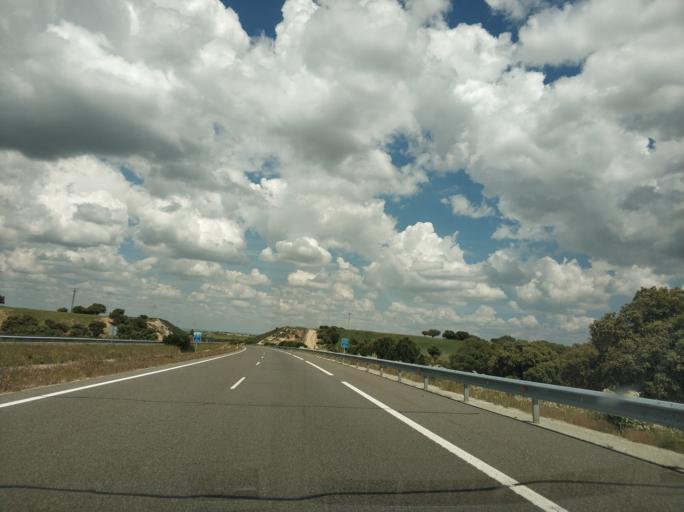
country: ES
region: Castille and Leon
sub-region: Provincia de Salamanca
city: Mozarbez
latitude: 40.8398
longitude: -5.6378
